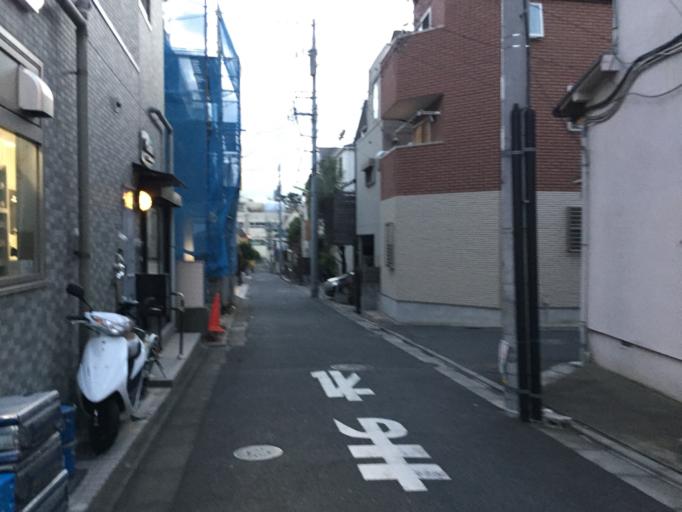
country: JP
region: Tokyo
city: Tokyo
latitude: 35.6408
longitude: 139.6743
